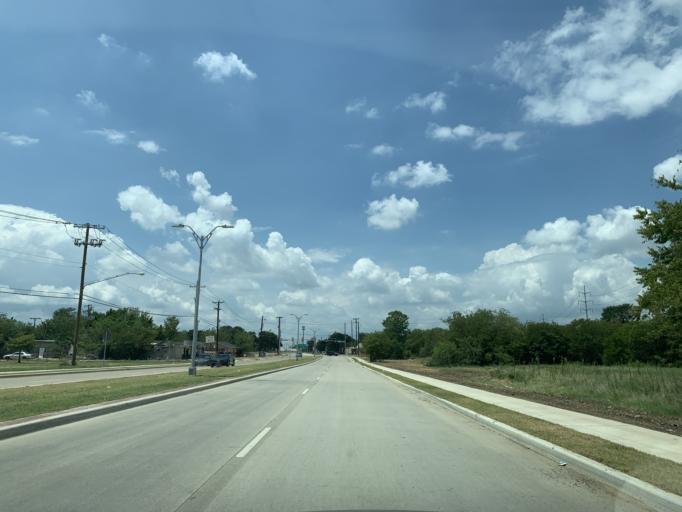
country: US
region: Texas
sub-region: Tarrant County
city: Forest Hill
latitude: 32.7310
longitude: -97.2428
